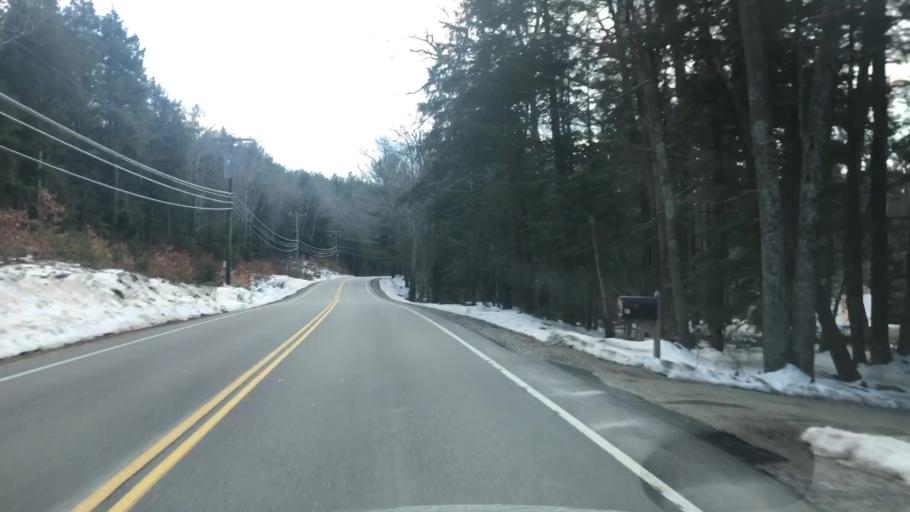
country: US
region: New Hampshire
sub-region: Hillsborough County
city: Mont Vernon
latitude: 42.8744
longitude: -71.6689
